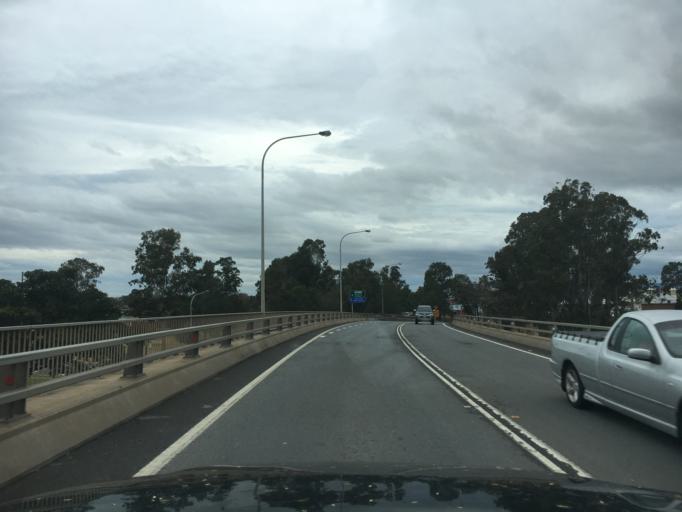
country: AU
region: New South Wales
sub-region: Singleton
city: Singleton
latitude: -32.5583
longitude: 151.1730
